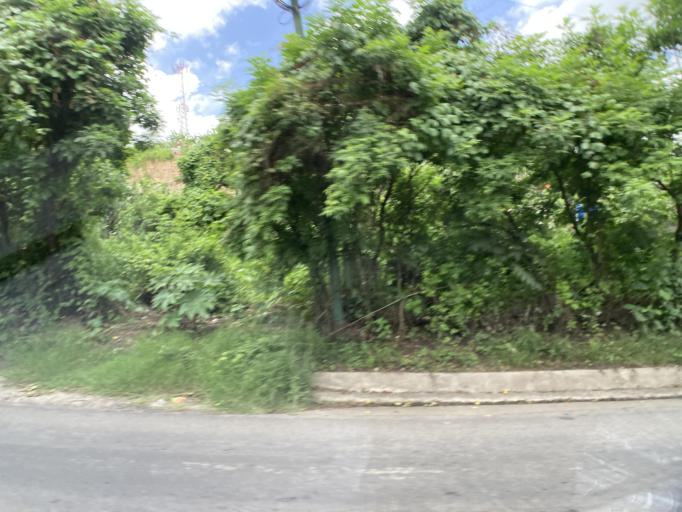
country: GT
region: Guatemala
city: Amatitlan
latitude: 14.4610
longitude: -90.5802
